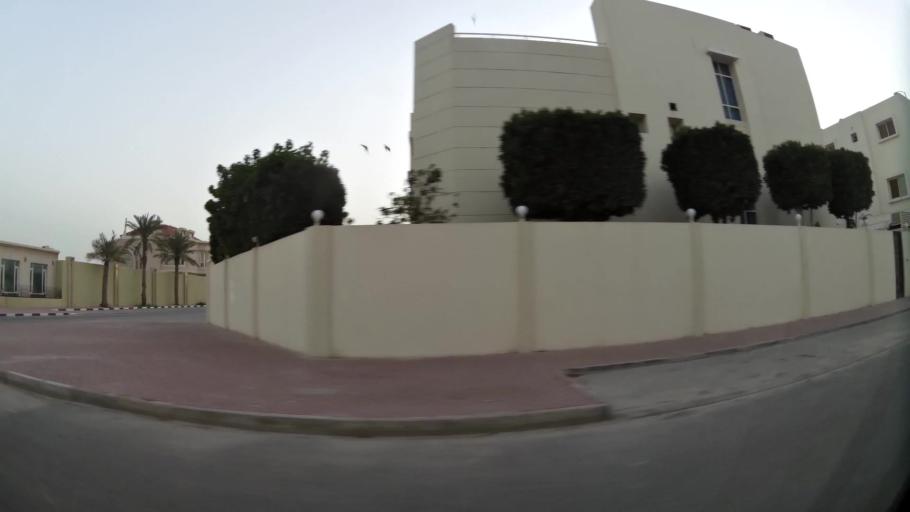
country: QA
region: Baladiyat ar Rayyan
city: Ar Rayyan
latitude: 25.2517
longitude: 51.4637
